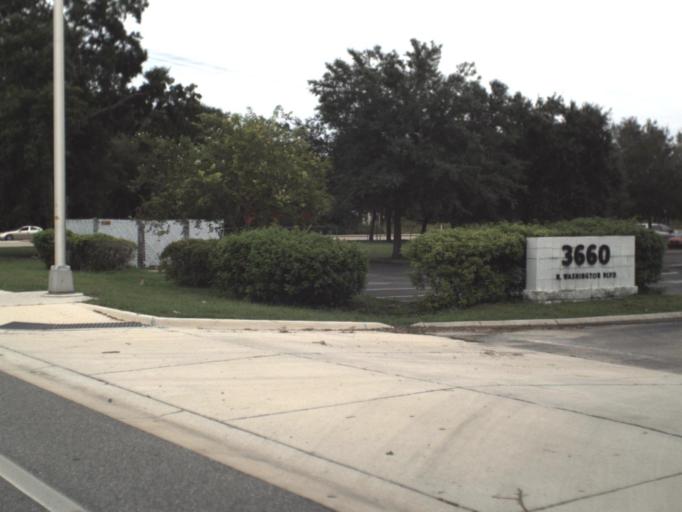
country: US
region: Florida
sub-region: Sarasota County
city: North Sarasota
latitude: 27.3664
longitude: -82.5306
